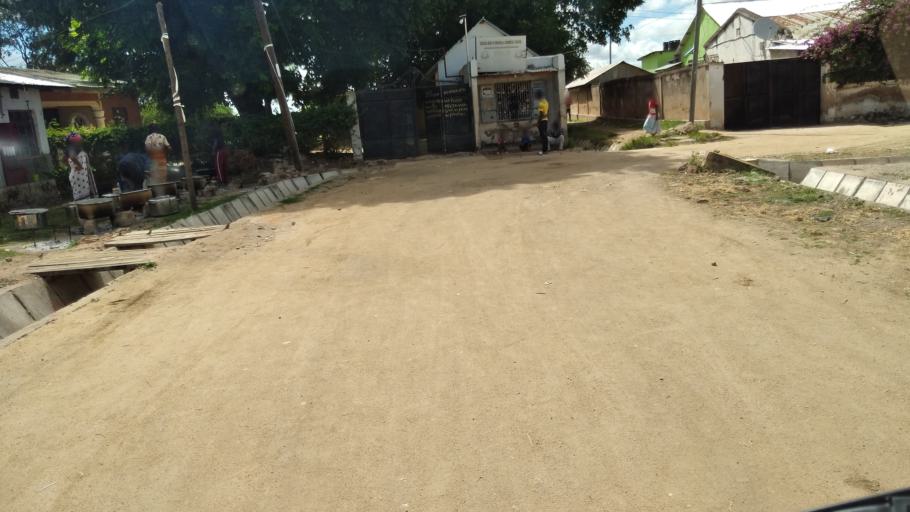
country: TZ
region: Dodoma
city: Dodoma
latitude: -6.1719
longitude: 35.7528
